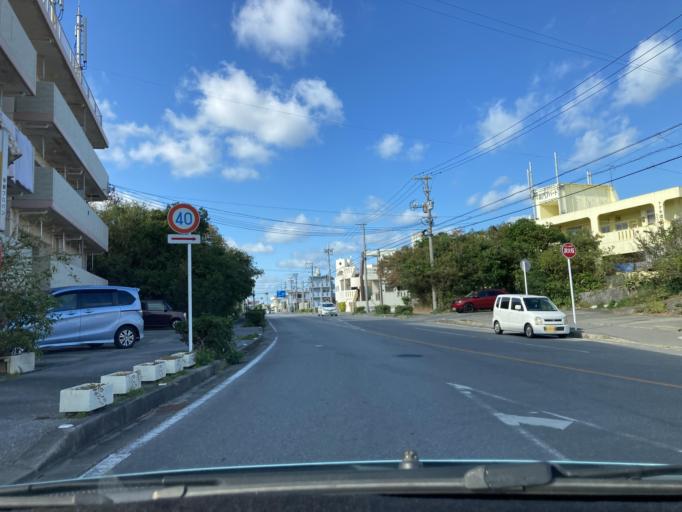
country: JP
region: Okinawa
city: Katsuren-haebaru
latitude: 26.3055
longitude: 127.9150
